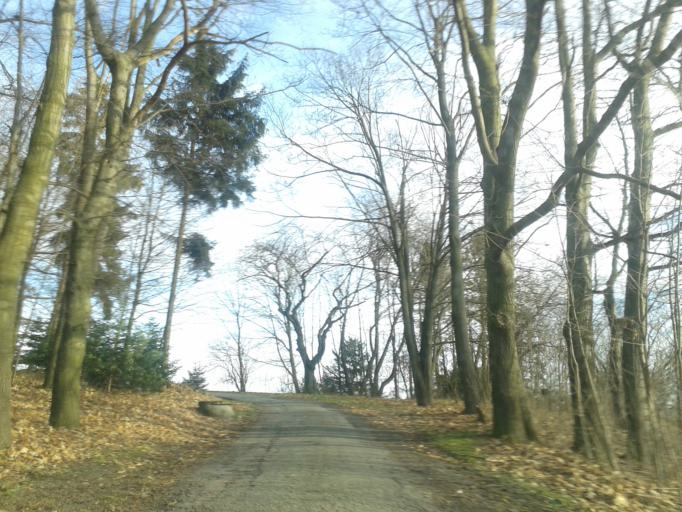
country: DE
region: Saxony
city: Eibau
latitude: 50.9823
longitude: 14.6720
